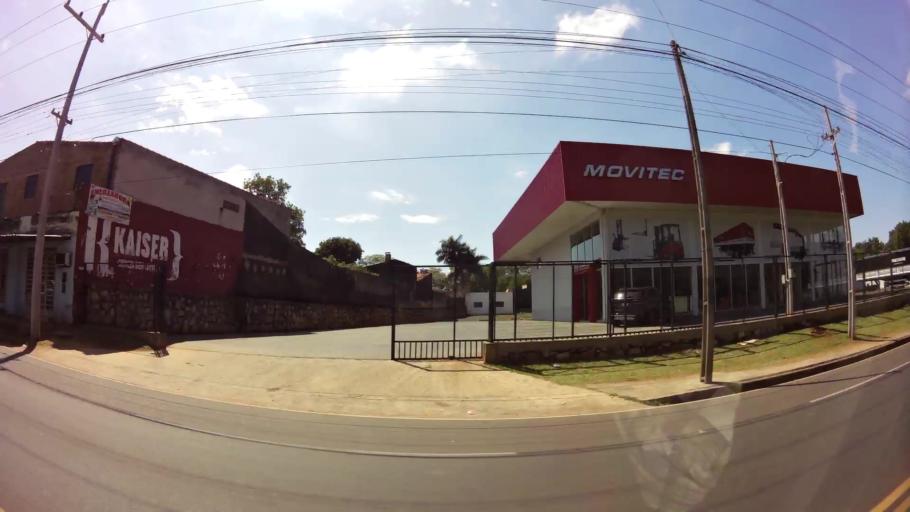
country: PY
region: Central
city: San Lorenzo
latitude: -25.3154
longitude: -57.5071
